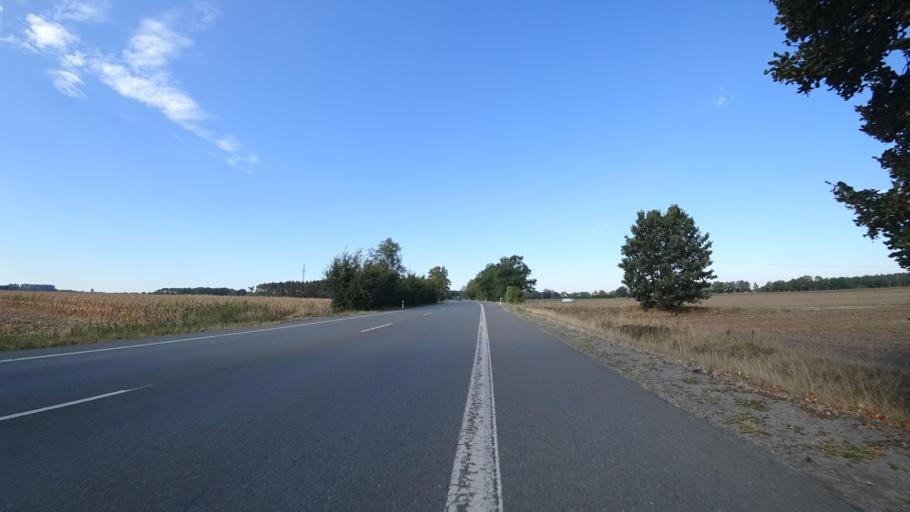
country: DE
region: North Rhine-Westphalia
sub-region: Regierungsbezirk Detmold
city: Rheda-Wiedenbruck
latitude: 51.8984
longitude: 8.3062
